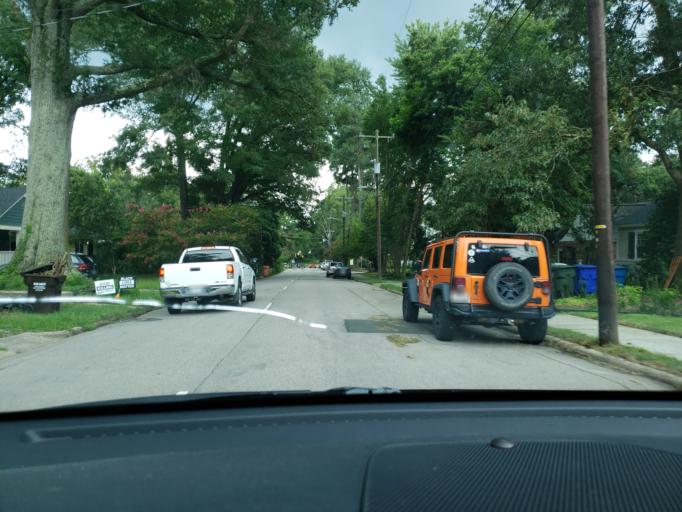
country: US
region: North Carolina
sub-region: Durham County
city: Durham
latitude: 35.9860
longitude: -78.9120
